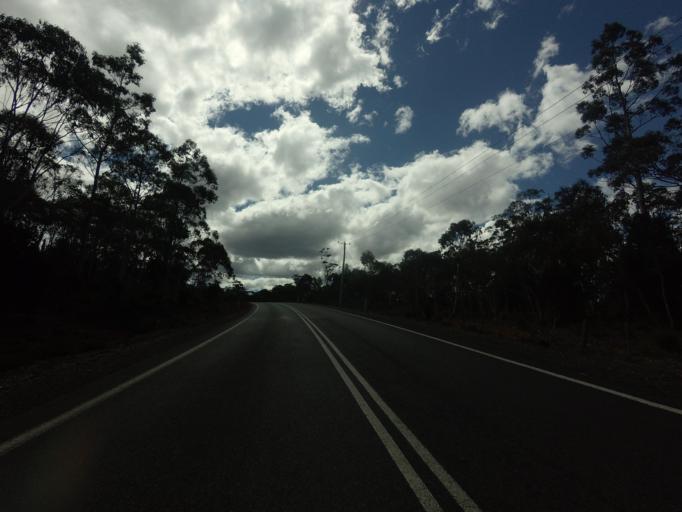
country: AU
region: Tasmania
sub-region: Northern Midlands
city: Evandale
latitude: -42.0246
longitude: 147.7733
